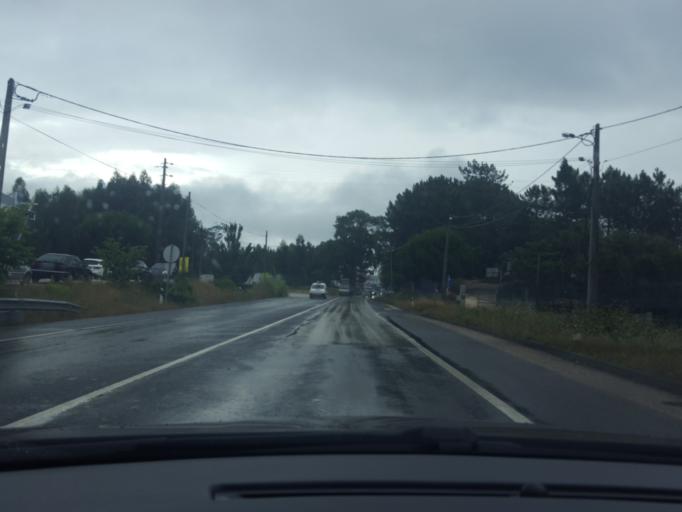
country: PT
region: Leiria
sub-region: Leiria
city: Leiria
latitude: 39.7355
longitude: -8.7677
